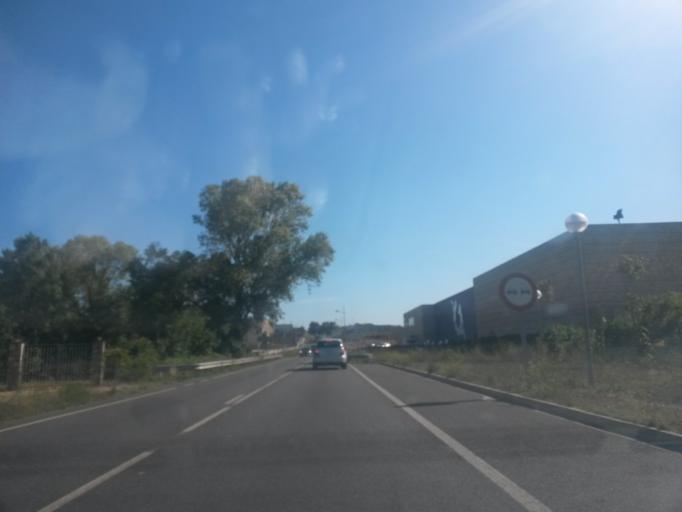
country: ES
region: Catalonia
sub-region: Provincia de Girona
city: Palafrugell
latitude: 41.9301
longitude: 3.1576
